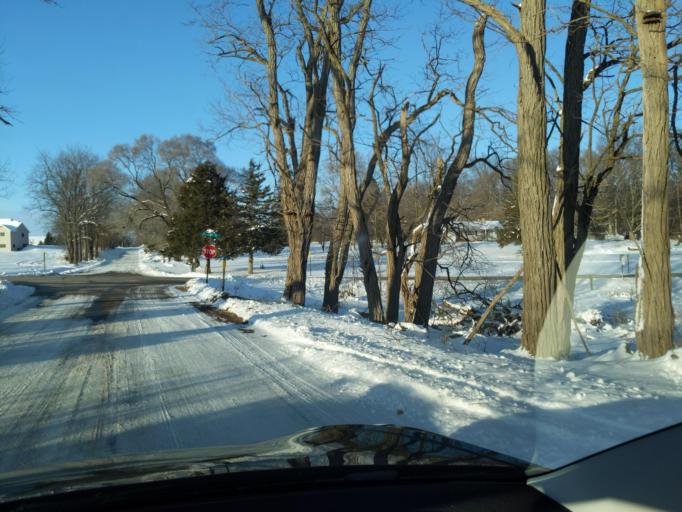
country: US
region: Michigan
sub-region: Ingham County
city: Stockbridge
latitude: 42.4675
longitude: -84.1192
